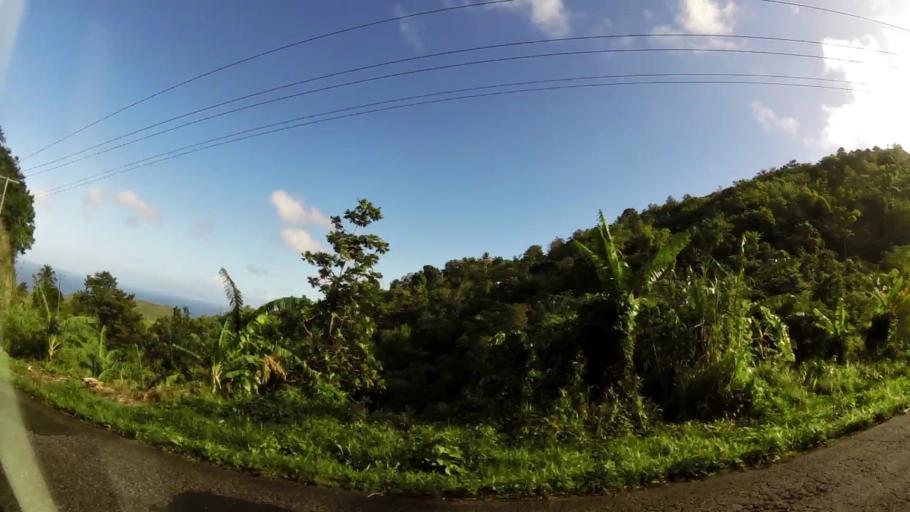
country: LC
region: Anse-la-Raye
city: Canaries
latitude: 13.9141
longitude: -61.0483
